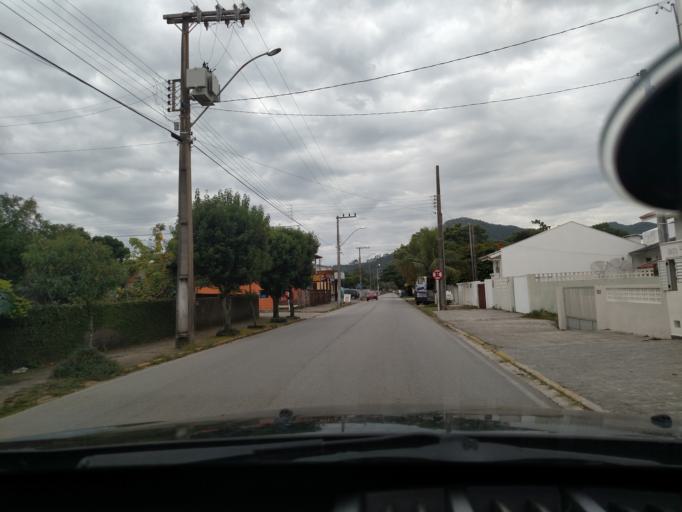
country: BR
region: Santa Catarina
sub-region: Porto Belo
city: Porto Belo
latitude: -27.1919
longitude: -48.5042
